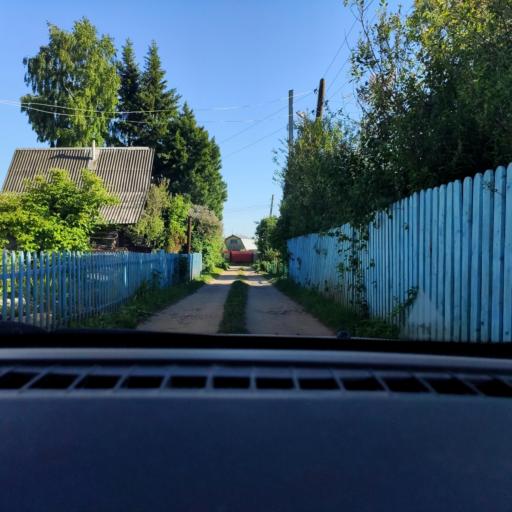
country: RU
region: Perm
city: Overyata
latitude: 58.1171
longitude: 55.8833
